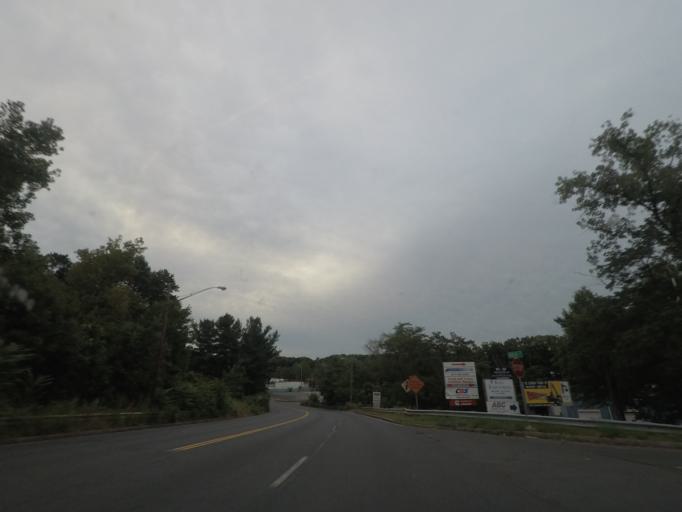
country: US
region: Massachusetts
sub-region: Hampden County
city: Ludlow
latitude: 42.1501
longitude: -72.5261
